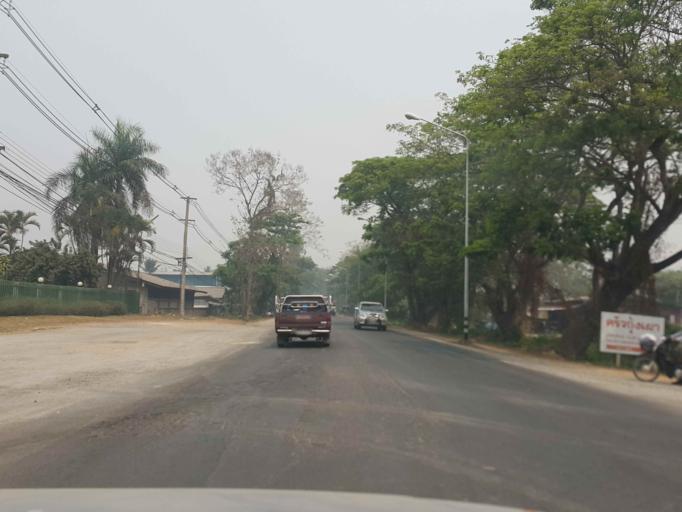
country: TH
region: Chiang Mai
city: San Sai
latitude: 18.9615
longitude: 98.9838
